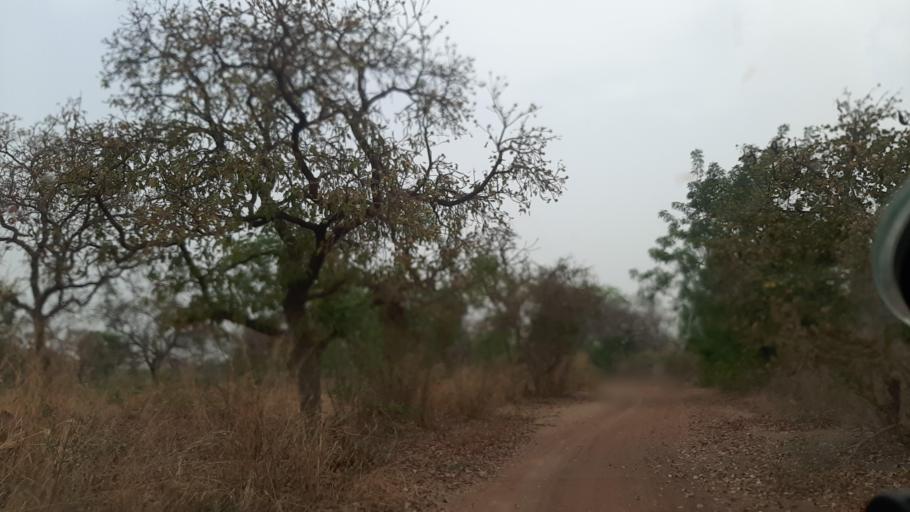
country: BF
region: Boucle du Mouhoun
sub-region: Province des Banwa
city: Salanso
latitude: 11.8486
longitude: -4.4215
